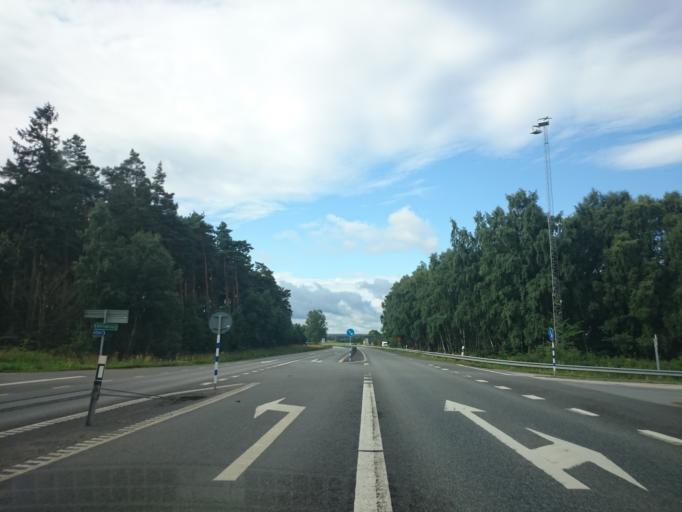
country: SE
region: Skane
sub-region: Kristianstads Kommun
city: Norra Asum
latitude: 55.9664
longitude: 14.0730
